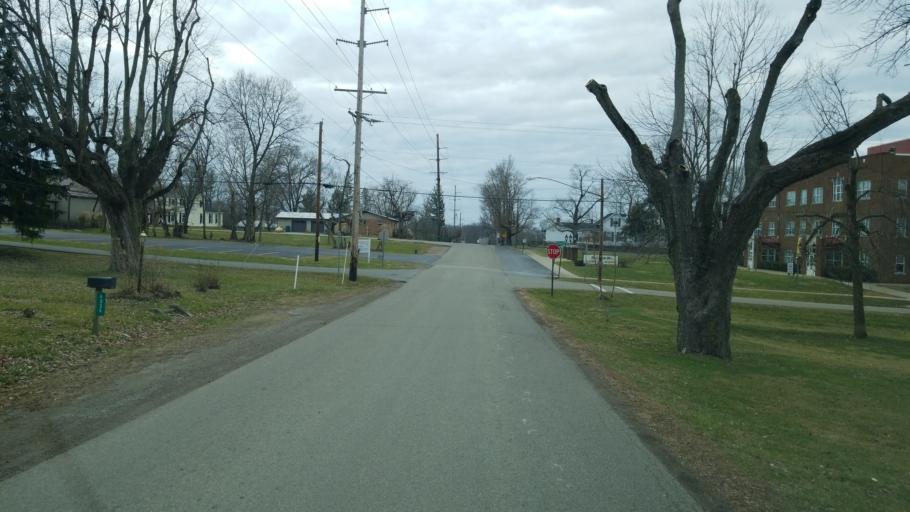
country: US
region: Ohio
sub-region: Highland County
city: Greenfield
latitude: 39.3354
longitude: -83.3089
